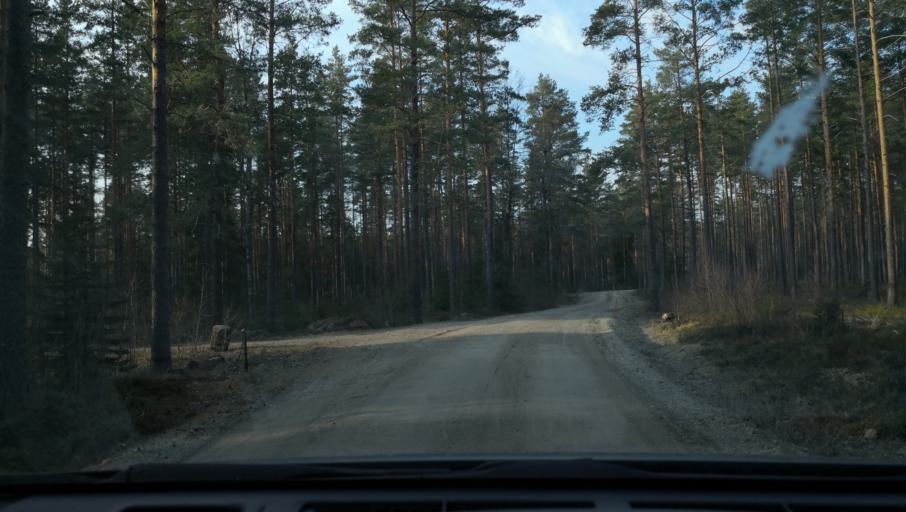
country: SE
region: OErebro
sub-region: Orebro Kommun
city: Hovsta
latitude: 59.3606
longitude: 15.3284
